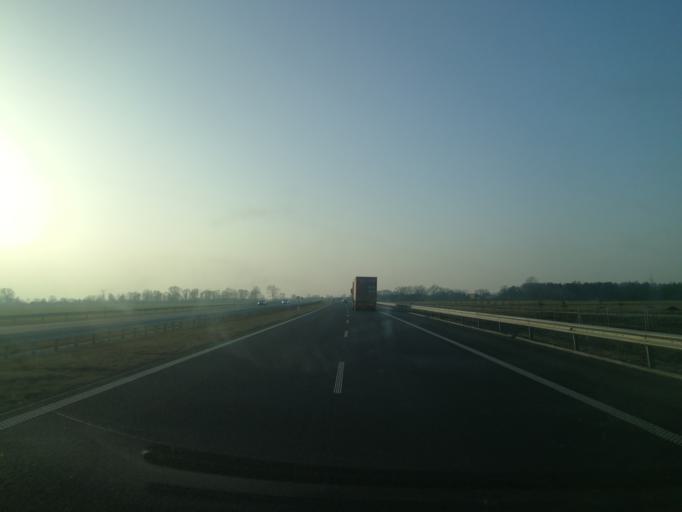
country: PL
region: Pomeranian Voivodeship
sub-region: Powiat nowodworski
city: Nowy Dwor Gdanski
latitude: 54.1723
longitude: 19.2135
